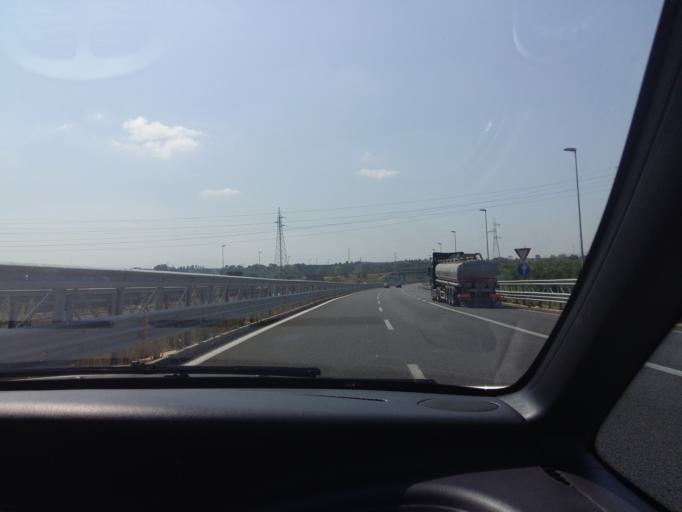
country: IT
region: Calabria
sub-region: Provincia di Reggio Calabria
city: Rosarno
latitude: 38.4786
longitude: 16.0002
